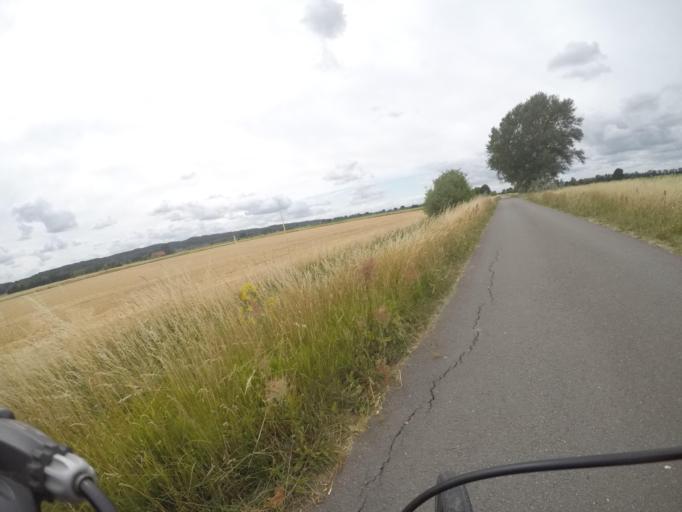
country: DE
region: Lower Saxony
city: Neu Darchau
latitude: 53.2186
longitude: 10.9612
